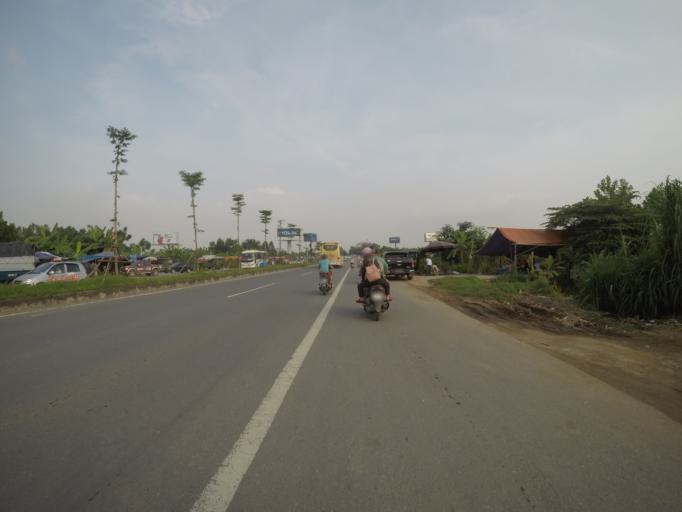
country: VN
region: Ha Noi
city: Me Linh
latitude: 21.2178
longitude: 105.7758
